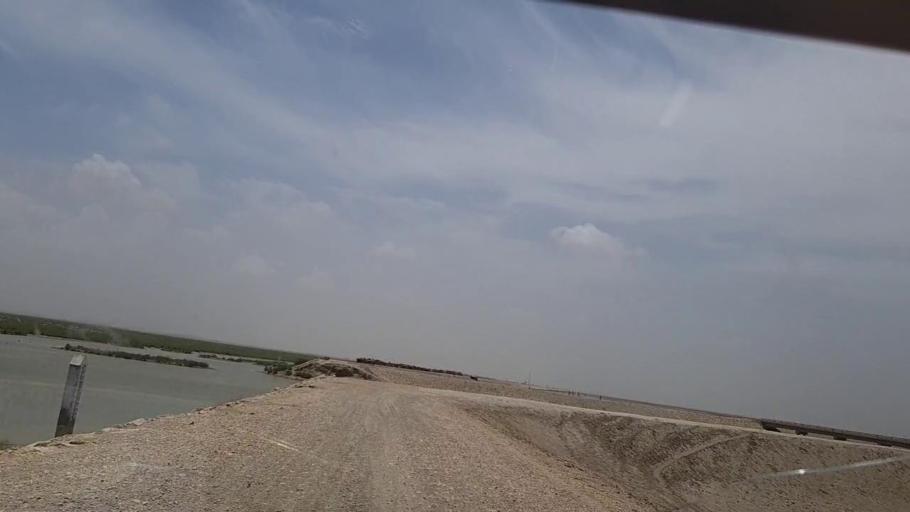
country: PK
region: Sindh
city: Bhan
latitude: 26.5092
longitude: 67.6261
